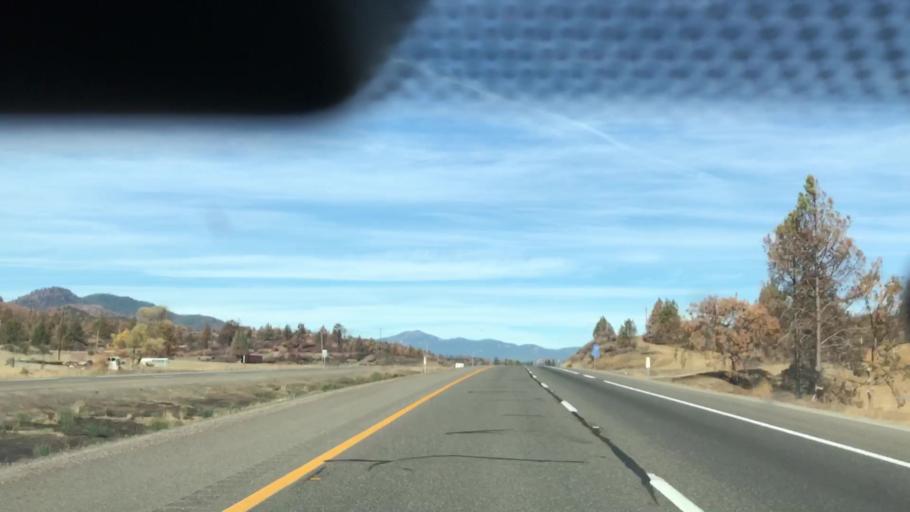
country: US
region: California
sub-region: Siskiyou County
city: Montague
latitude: 41.8932
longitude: -122.5622
